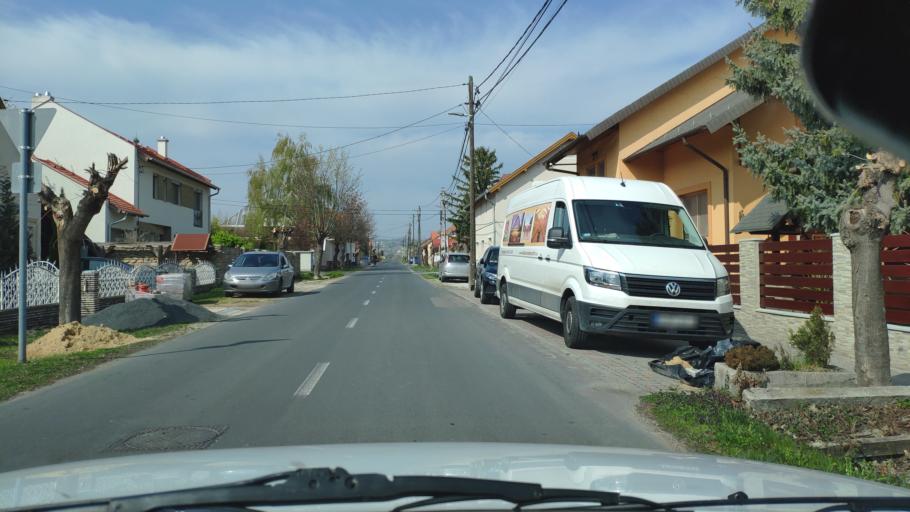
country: HU
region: Zala
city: Keszthely
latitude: 46.7691
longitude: 17.2634
